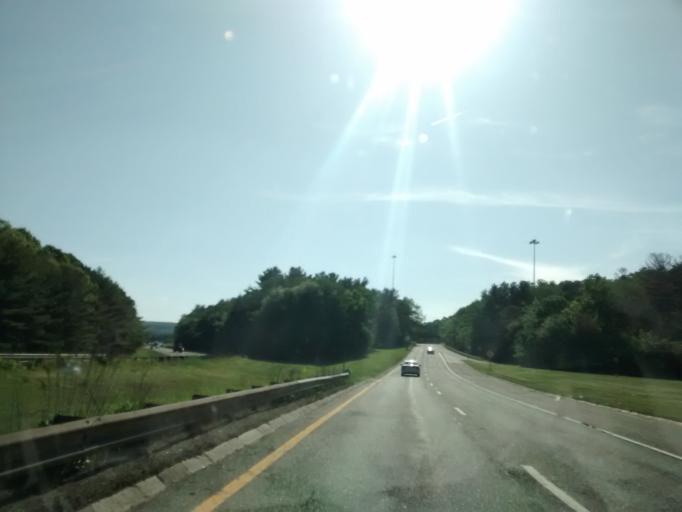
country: US
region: Massachusetts
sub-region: Worcester County
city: Sturbridge
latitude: 42.1166
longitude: -72.0706
